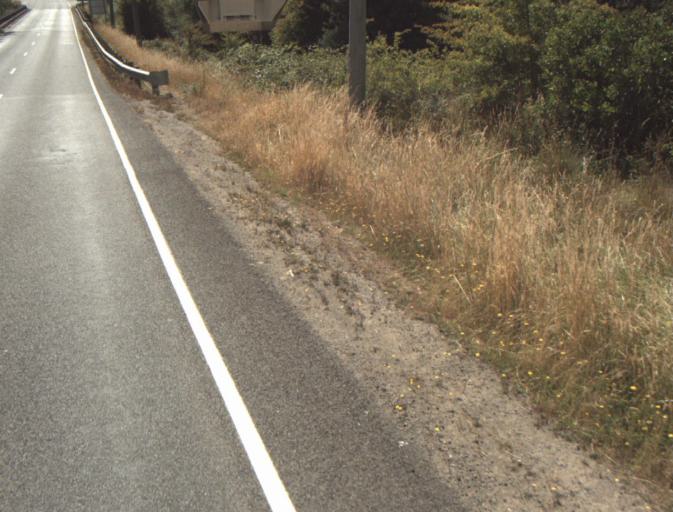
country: AU
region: Tasmania
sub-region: Launceston
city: Newstead
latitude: -41.3899
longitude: 147.2997
